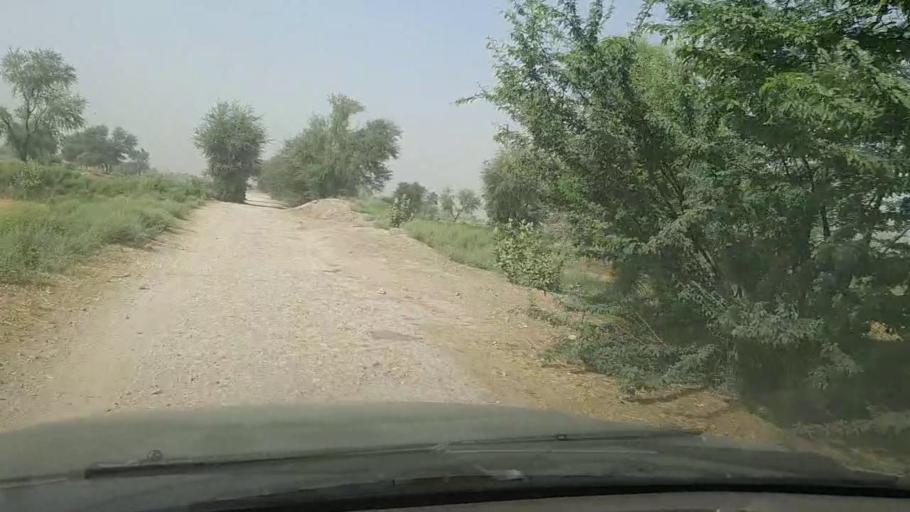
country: PK
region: Sindh
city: Shikarpur
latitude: 27.9090
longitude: 68.6008
